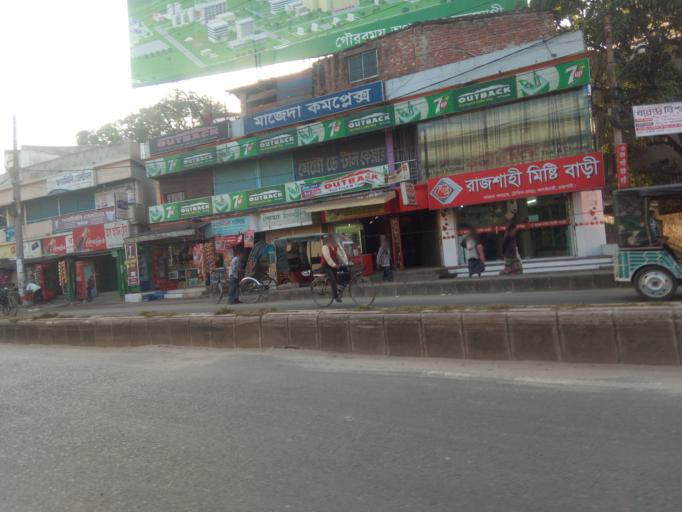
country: BD
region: Rajshahi
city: Rajshahi
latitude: 24.3617
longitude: 88.6274
